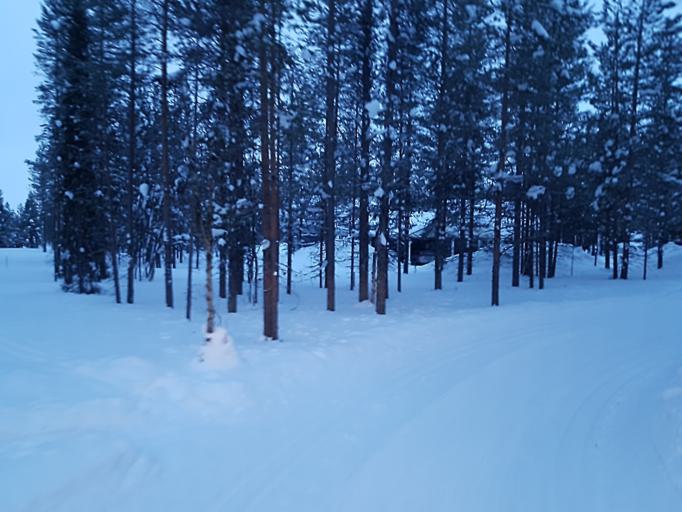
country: FI
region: Lapland
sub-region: Tunturi-Lappi
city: Kolari
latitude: 67.6229
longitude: 24.1568
